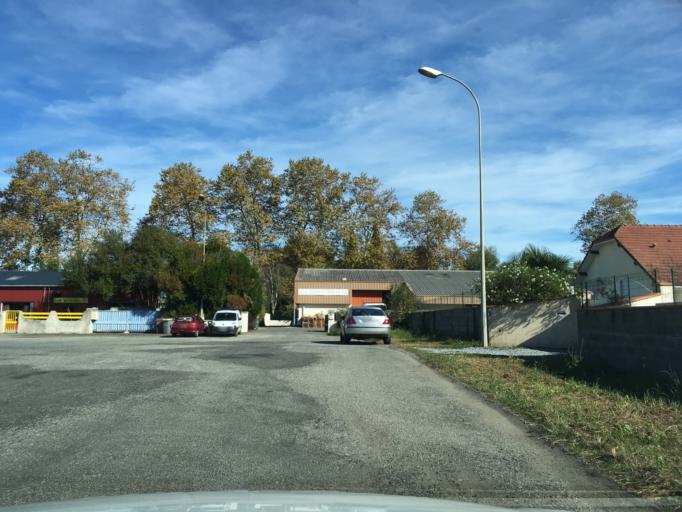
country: FR
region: Aquitaine
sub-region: Departement des Pyrenees-Atlantiques
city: Buros
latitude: 43.3222
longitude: -0.3157
